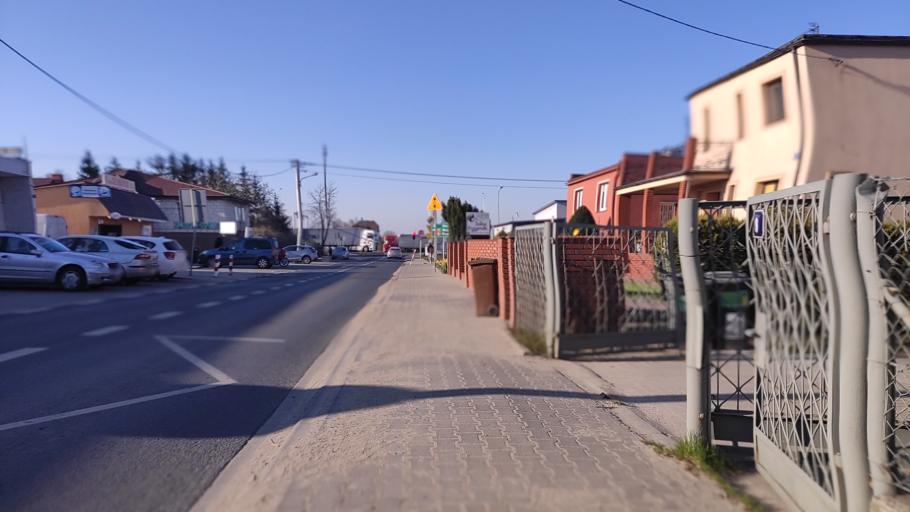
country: PL
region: Greater Poland Voivodeship
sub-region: Powiat poznanski
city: Kleszczewo
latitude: 52.3996
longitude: 17.1588
